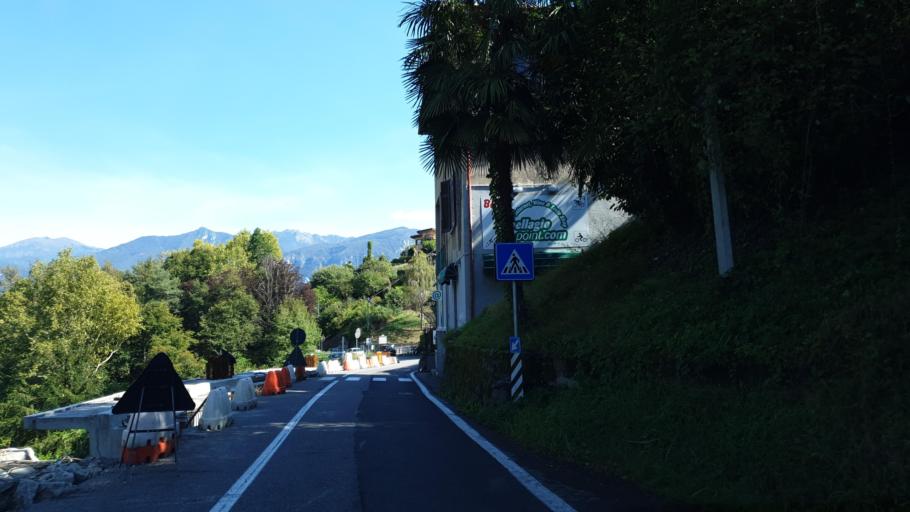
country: IT
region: Lombardy
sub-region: Provincia di Como
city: Cadenabbia
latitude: 45.9702
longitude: 9.2389
